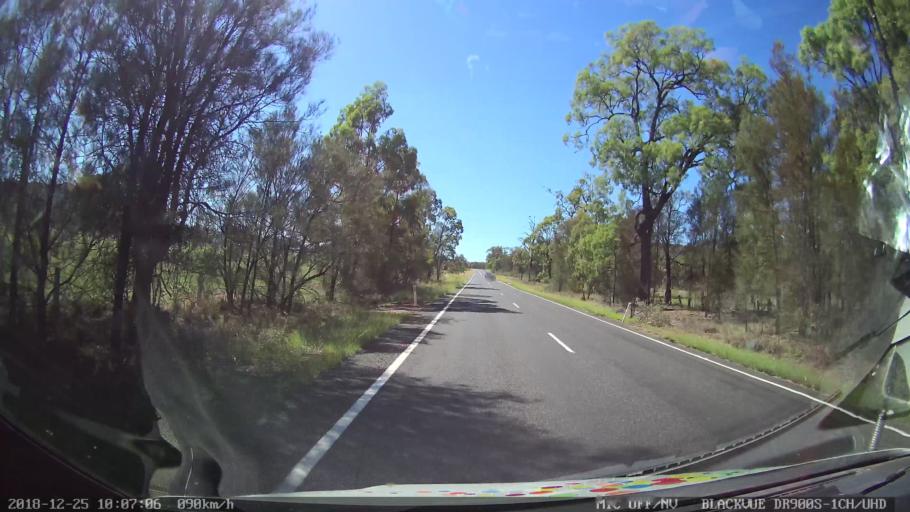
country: AU
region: New South Wales
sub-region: Upper Hunter Shire
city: Merriwa
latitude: -32.2672
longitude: 150.4953
